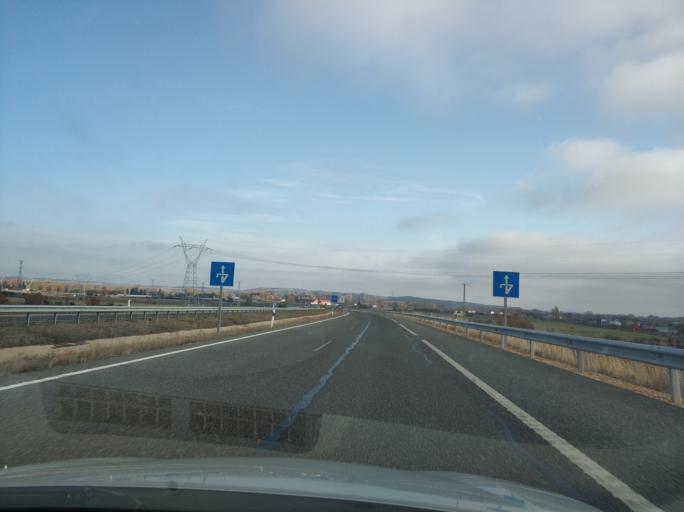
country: ES
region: Castille and Leon
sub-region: Provincia de Leon
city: Villaturiel
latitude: 42.5561
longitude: -5.4691
